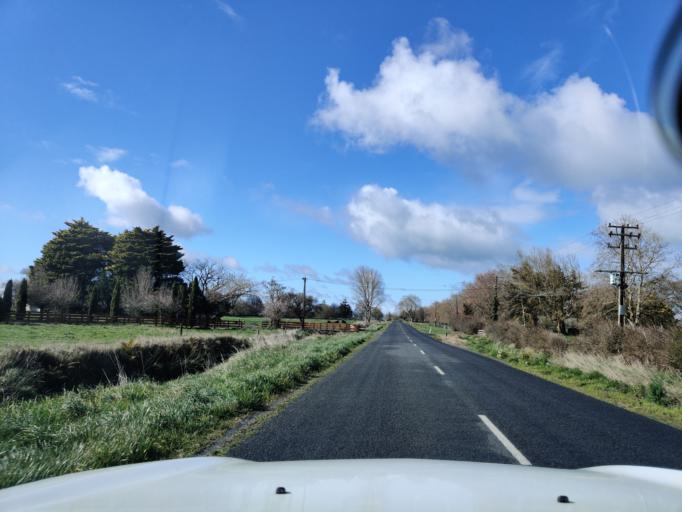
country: NZ
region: Waikato
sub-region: Waikato District
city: Ngaruawahia
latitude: -37.6094
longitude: 175.3086
